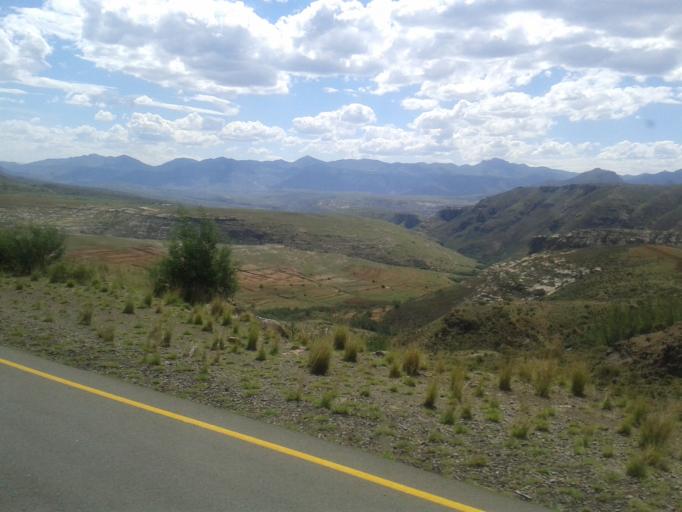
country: LS
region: Qacha's Nek
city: Qacha's Nek
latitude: -30.0490
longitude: 28.3068
